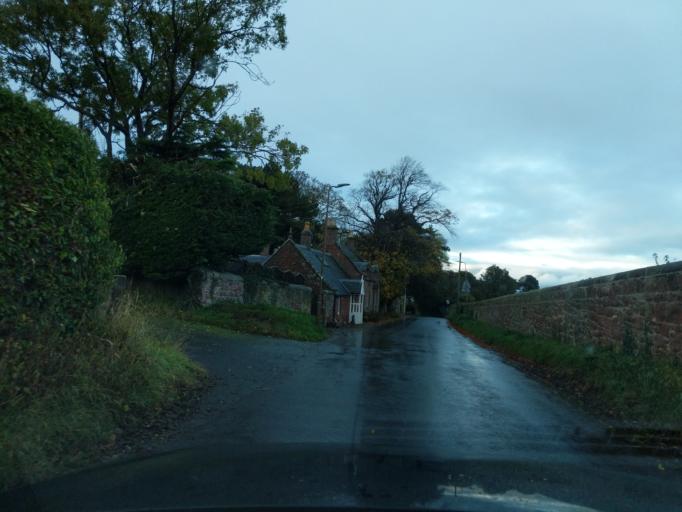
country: GB
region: Scotland
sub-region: East Lothian
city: Dunbar
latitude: 55.9729
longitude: -2.5227
